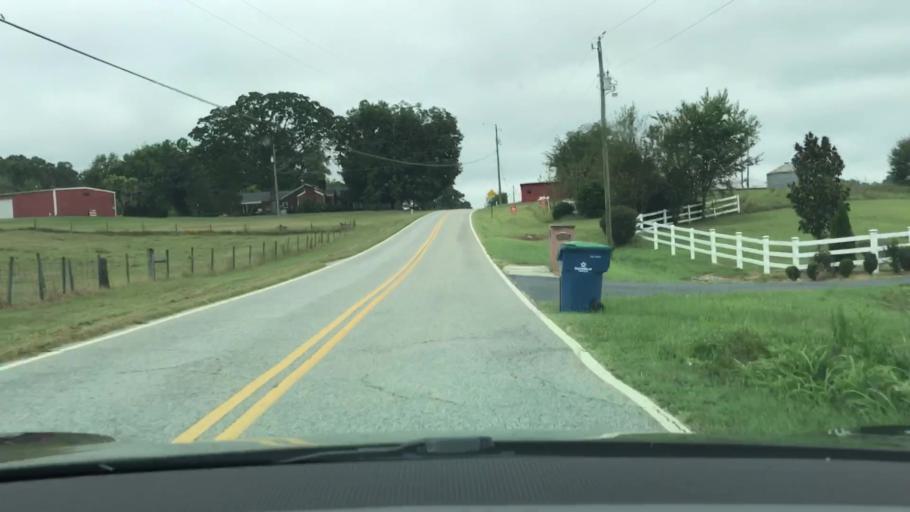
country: US
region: Georgia
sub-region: Barrow County
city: Auburn
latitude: 34.0446
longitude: -83.8095
